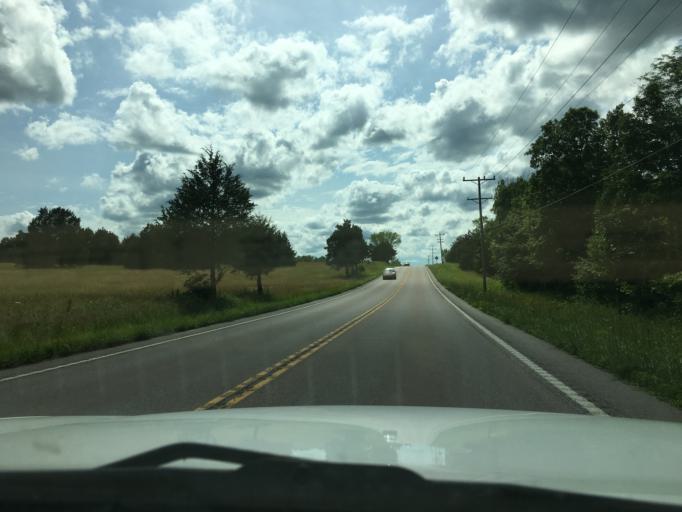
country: US
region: Missouri
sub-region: Franklin County
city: Gerald
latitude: 38.3875
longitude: -91.3866
